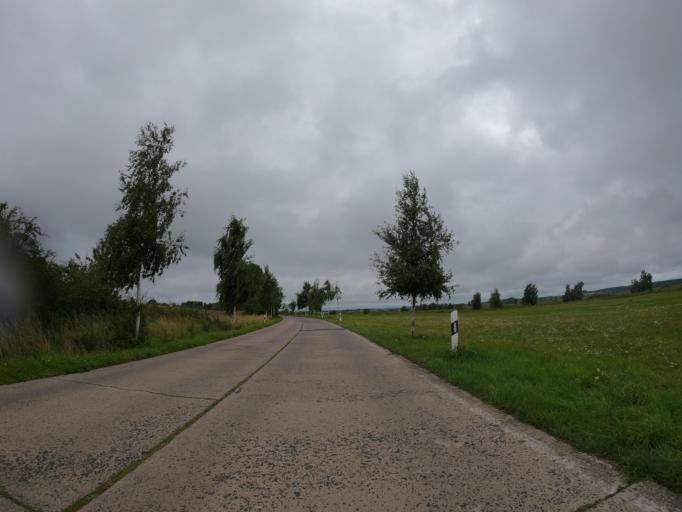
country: DE
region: Mecklenburg-Vorpommern
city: Ostseebad Gohren
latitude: 54.3075
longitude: 13.6957
